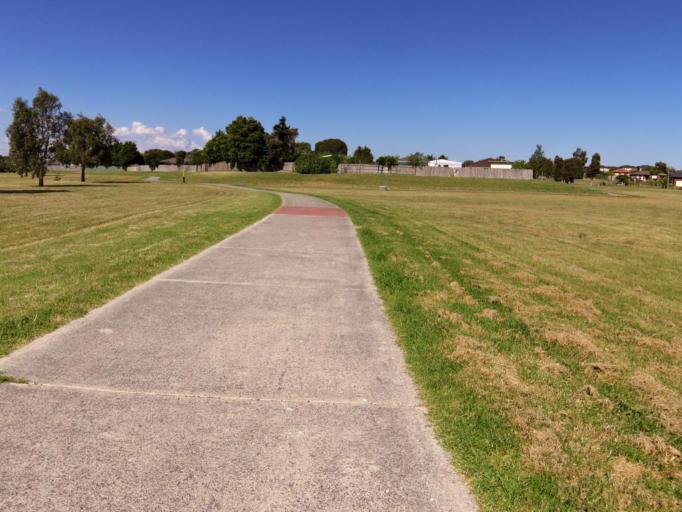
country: AU
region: Victoria
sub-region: Casey
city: Hampton Park
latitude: -38.0217
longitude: 145.2516
